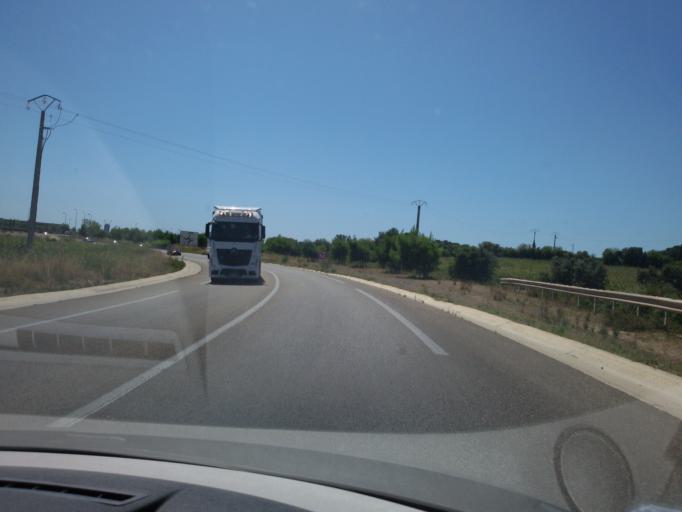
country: FR
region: Languedoc-Roussillon
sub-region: Departement de l'Herault
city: Frontignan
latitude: 43.4686
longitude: 3.7661
